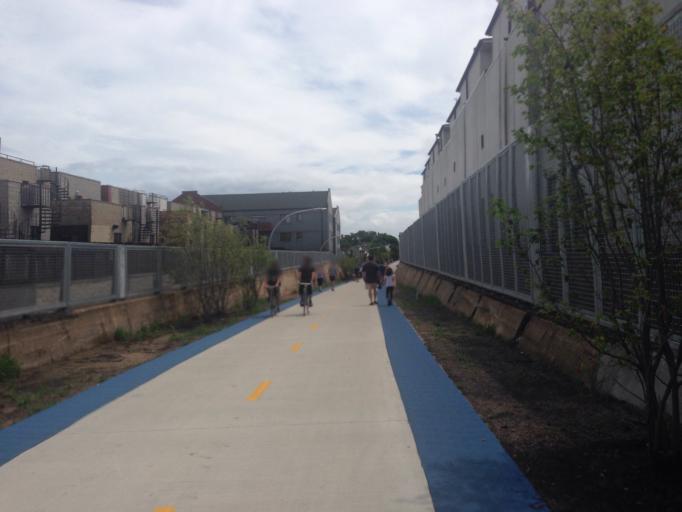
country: US
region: Illinois
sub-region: Cook County
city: Chicago
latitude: 41.9142
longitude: -87.6797
